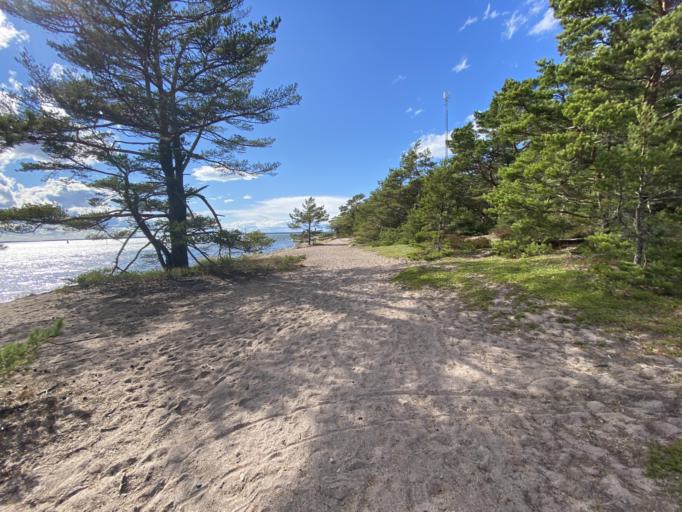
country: SE
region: Stockholm
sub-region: Varmdo Kommun
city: Holo
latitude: 59.2794
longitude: 18.9045
